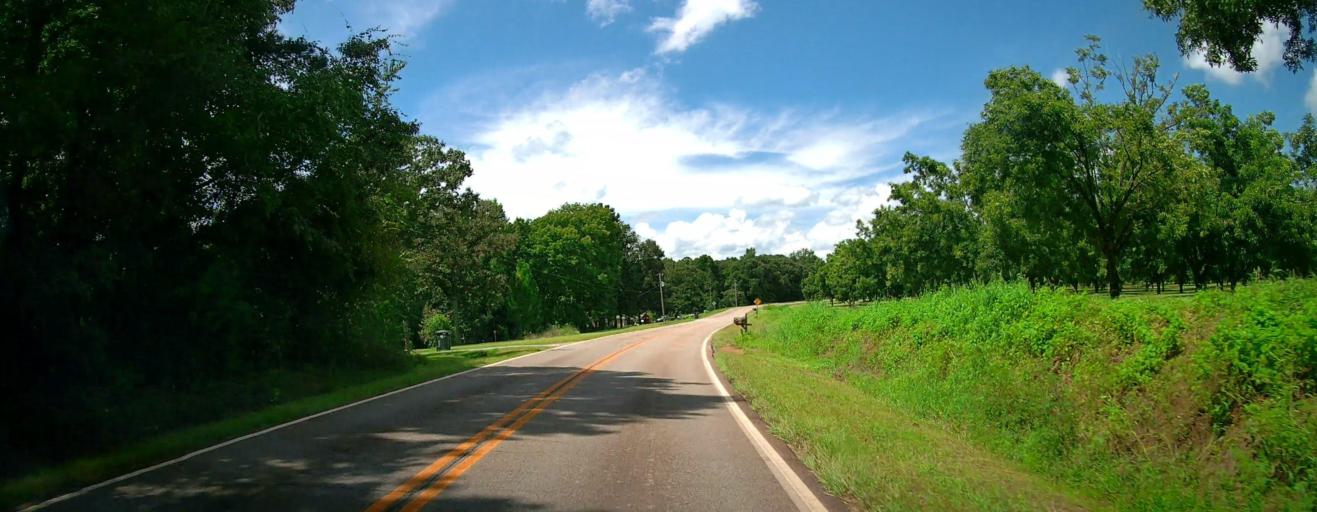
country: US
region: Georgia
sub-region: Houston County
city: Perry
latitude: 32.5219
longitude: -83.7996
